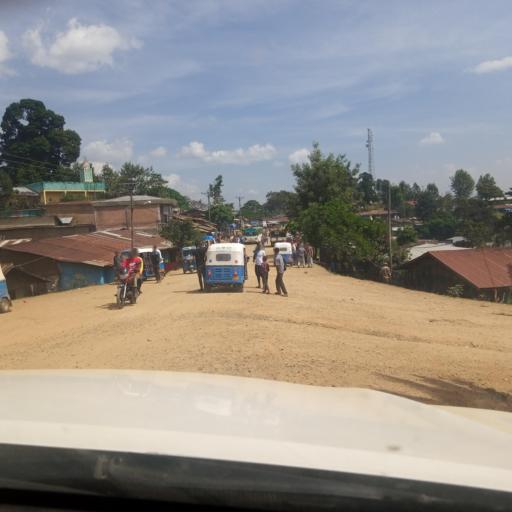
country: ET
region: Southern Nations, Nationalities, and People's Region
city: Mizan Teferi
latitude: 7.0559
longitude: 35.4990
